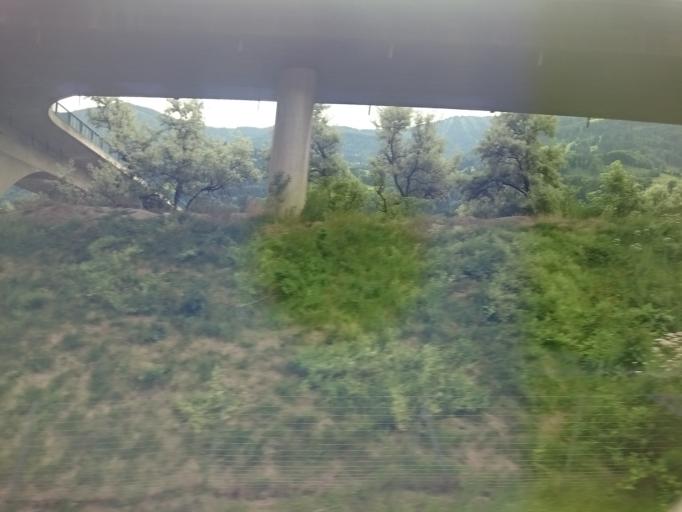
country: AT
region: Tyrol
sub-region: Politischer Bezirk Schwaz
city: Buch bei Jenbach
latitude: 47.3778
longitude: 11.7480
